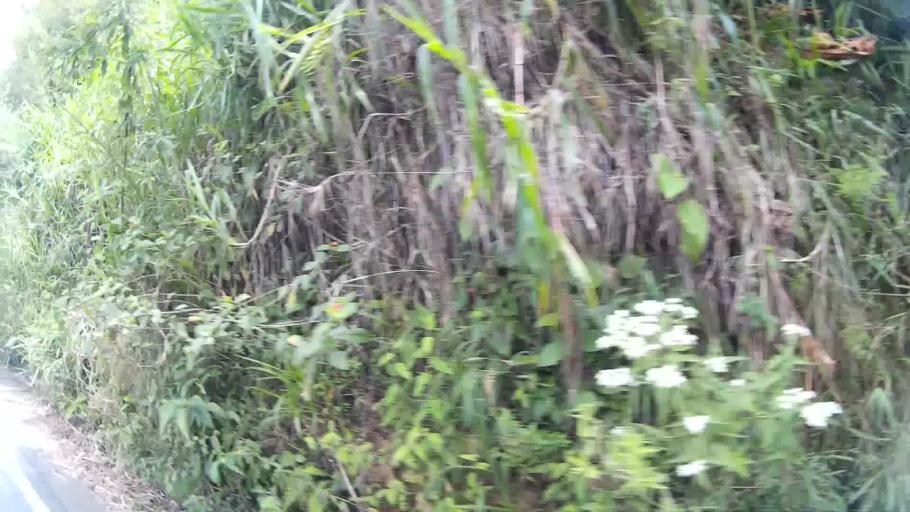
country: CO
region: Risaralda
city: Marsella
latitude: 4.8812
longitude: -75.7594
